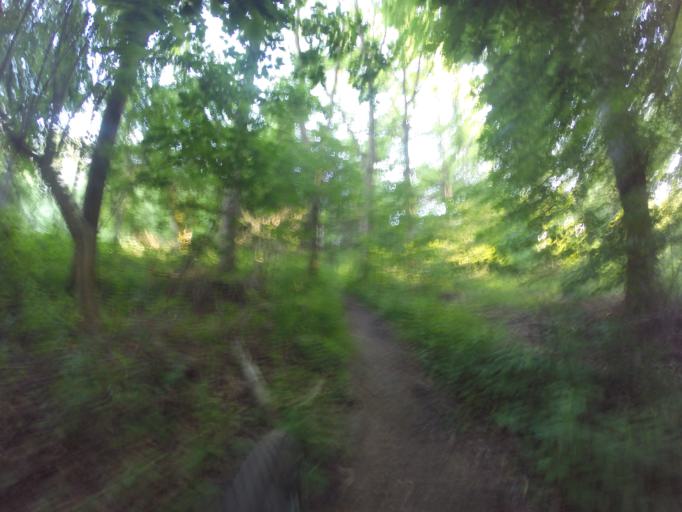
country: DK
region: Capital Region
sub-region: Hoje-Taastrup Kommune
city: Taastrup
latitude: 55.6829
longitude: 12.3158
